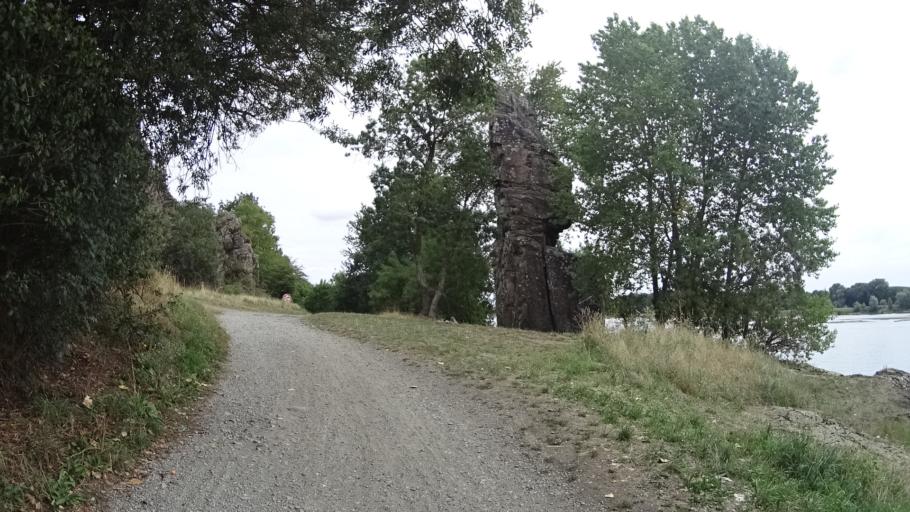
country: FR
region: Pays de la Loire
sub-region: Departement de Maine-et-Loire
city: Denee
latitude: 47.3960
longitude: -0.6288
